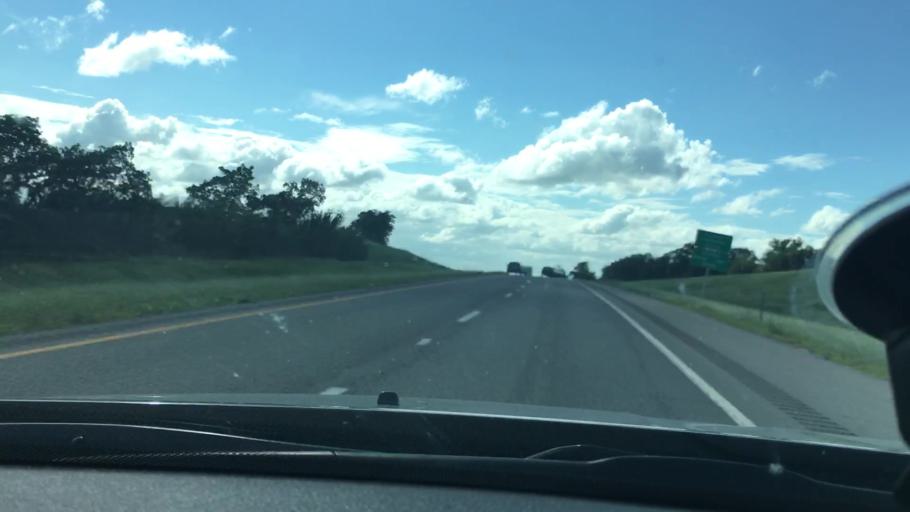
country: US
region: Oklahoma
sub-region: McIntosh County
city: Checotah
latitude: 35.4580
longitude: -95.4200
